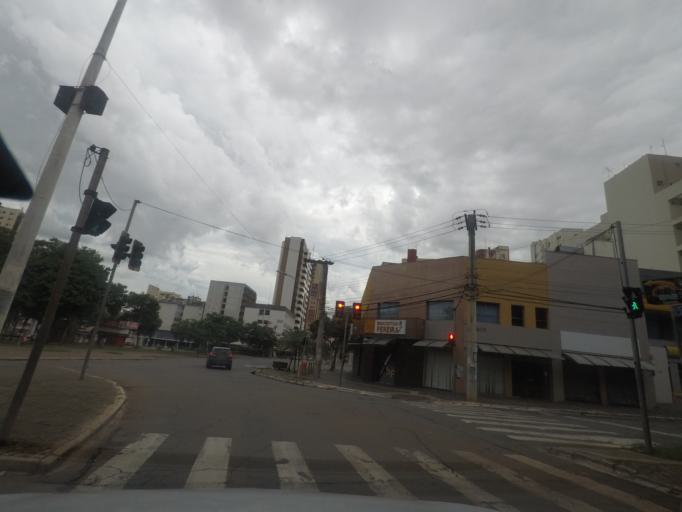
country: BR
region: Goias
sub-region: Goiania
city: Goiania
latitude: -16.6862
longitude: -49.2649
